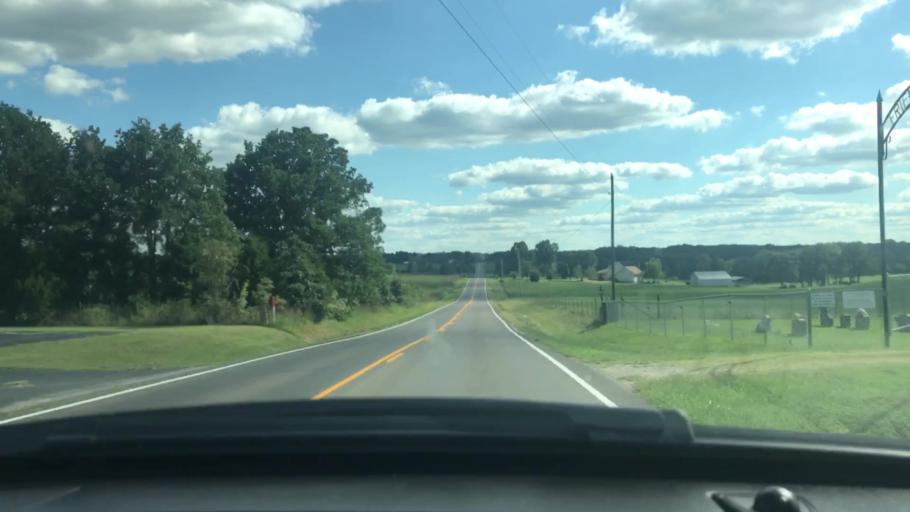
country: US
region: Missouri
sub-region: Wright County
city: Mountain Grove
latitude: 37.2466
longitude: -92.3003
